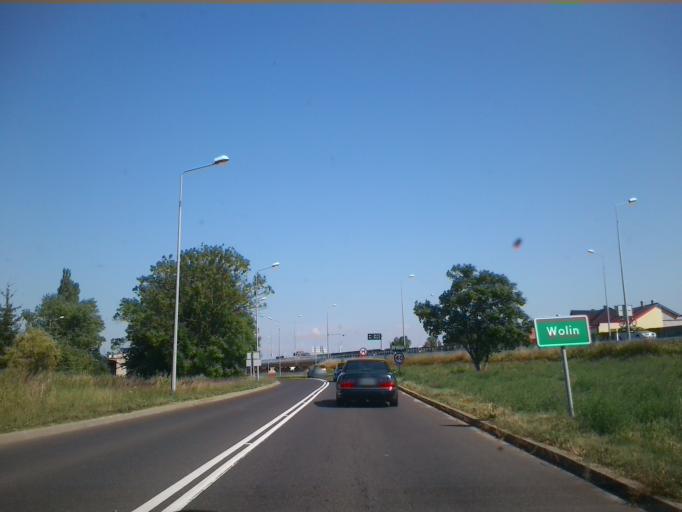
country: PL
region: West Pomeranian Voivodeship
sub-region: Powiat kamienski
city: Wolin
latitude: 53.8486
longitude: 14.6065
